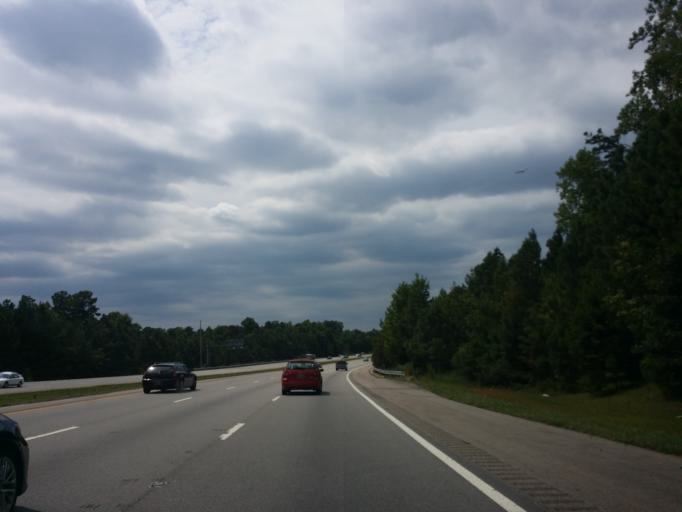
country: US
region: North Carolina
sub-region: Wake County
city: Morrisville
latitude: 35.9094
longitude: -78.7404
